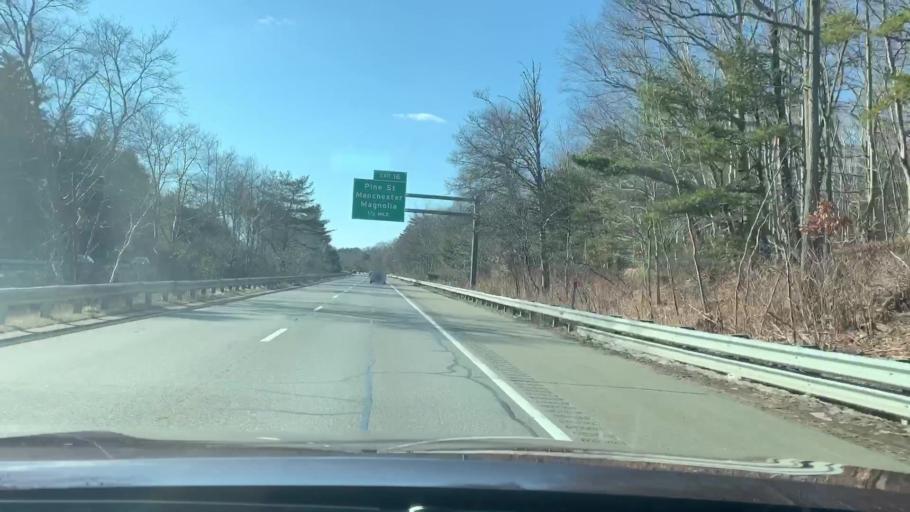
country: US
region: Massachusetts
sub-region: Essex County
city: Essex
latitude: 42.5916
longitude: -70.7780
